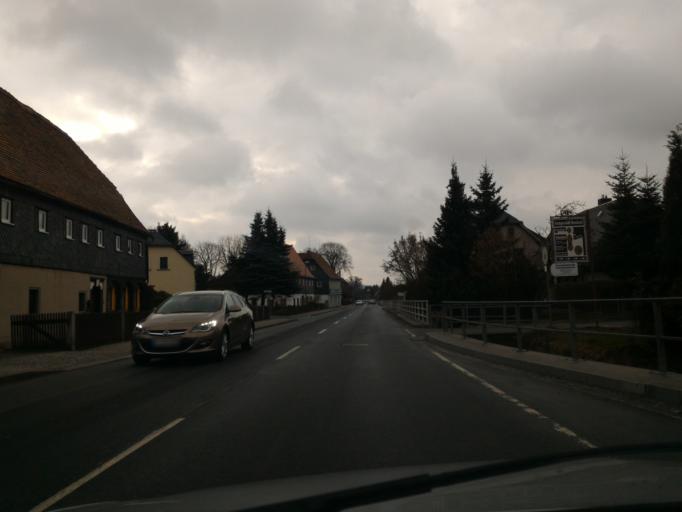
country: DE
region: Saxony
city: Eibau
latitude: 50.9915
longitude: 14.6489
